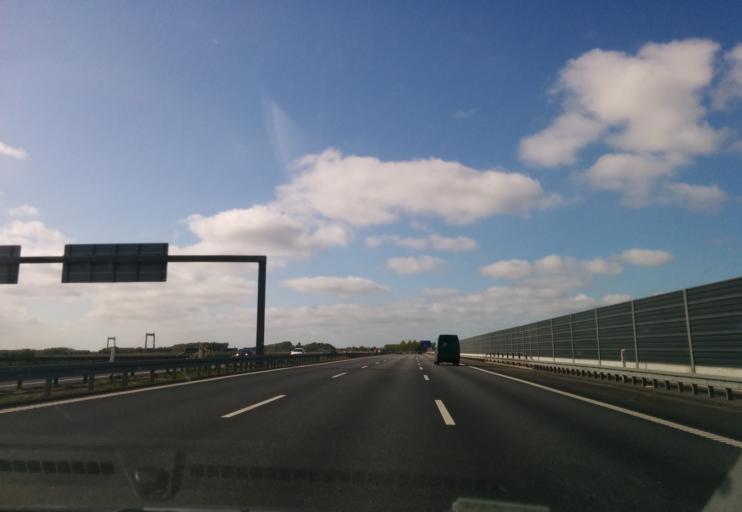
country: DK
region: South Denmark
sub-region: Middelfart Kommune
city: Strib
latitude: 55.5034
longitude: 9.7884
